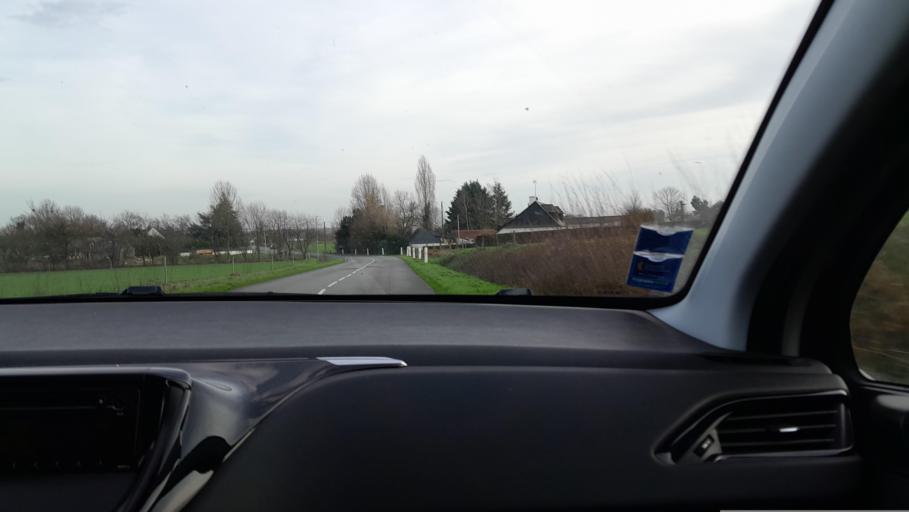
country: FR
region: Brittany
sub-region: Departement d'Ille-et-Vilaine
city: La Guerche-de-Bretagne
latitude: 47.9595
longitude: -1.1548
